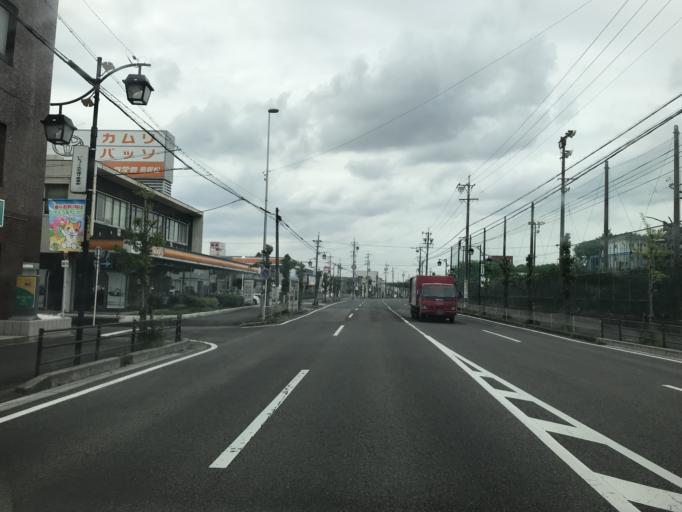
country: JP
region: Aichi
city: Kasugai
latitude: 35.2404
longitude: 136.9677
